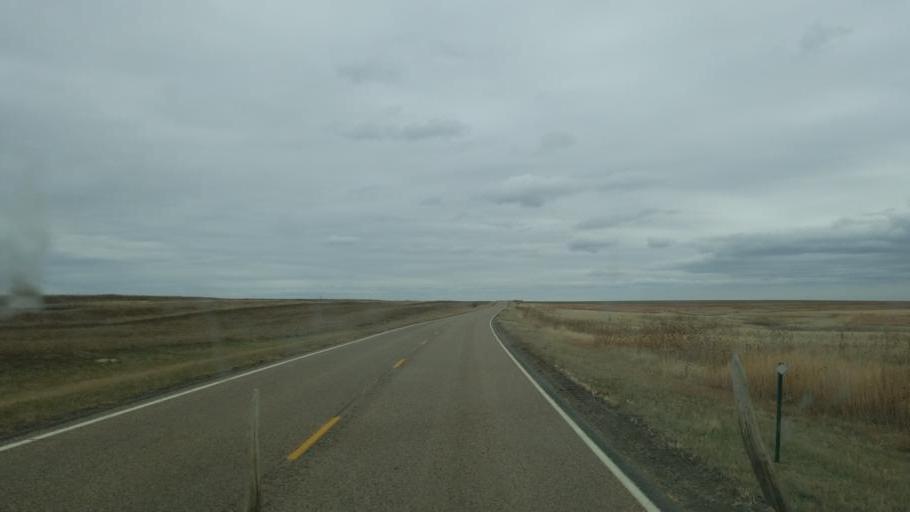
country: US
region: Colorado
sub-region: Cheyenne County
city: Cheyenne Wells
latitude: 38.8485
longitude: -102.1526
